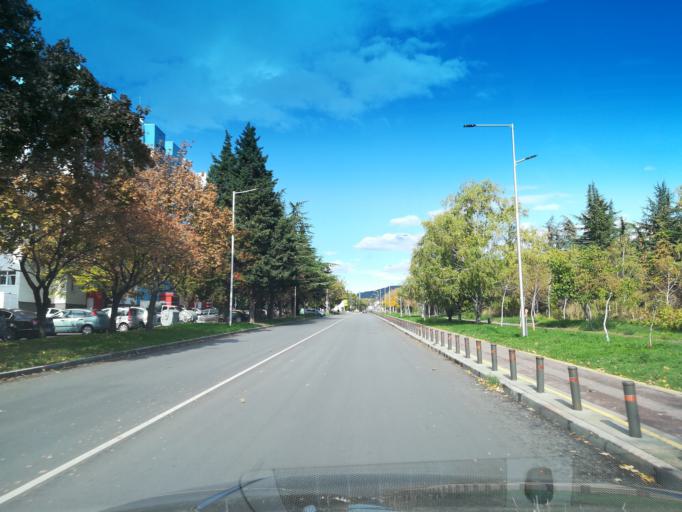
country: BG
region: Stara Zagora
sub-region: Obshtina Stara Zagora
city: Stara Zagora
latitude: 42.4364
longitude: 25.6364
